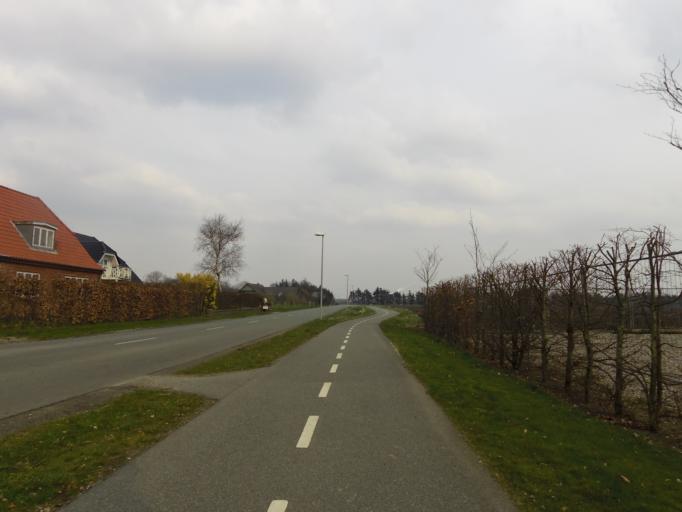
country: DK
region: South Denmark
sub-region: Esbjerg Kommune
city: Ribe
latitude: 55.3580
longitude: 8.7417
